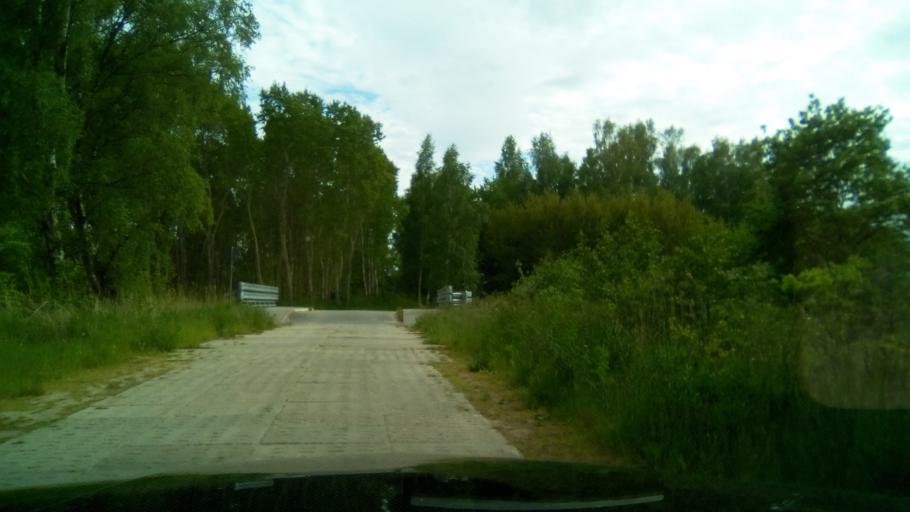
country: PL
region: Pomeranian Voivodeship
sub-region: Powiat pucki
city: Krokowa
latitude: 54.8272
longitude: 18.0930
